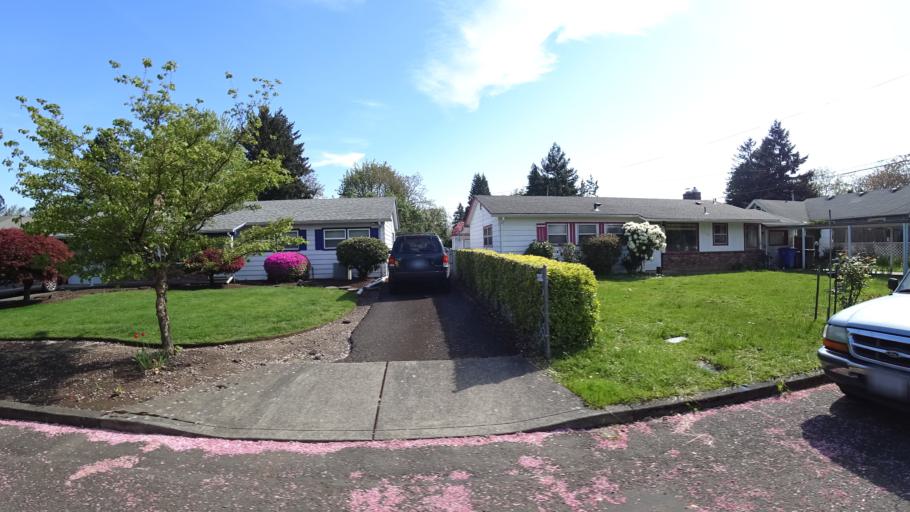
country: US
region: Oregon
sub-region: Clackamas County
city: Milwaukie
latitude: 45.4569
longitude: -122.6241
